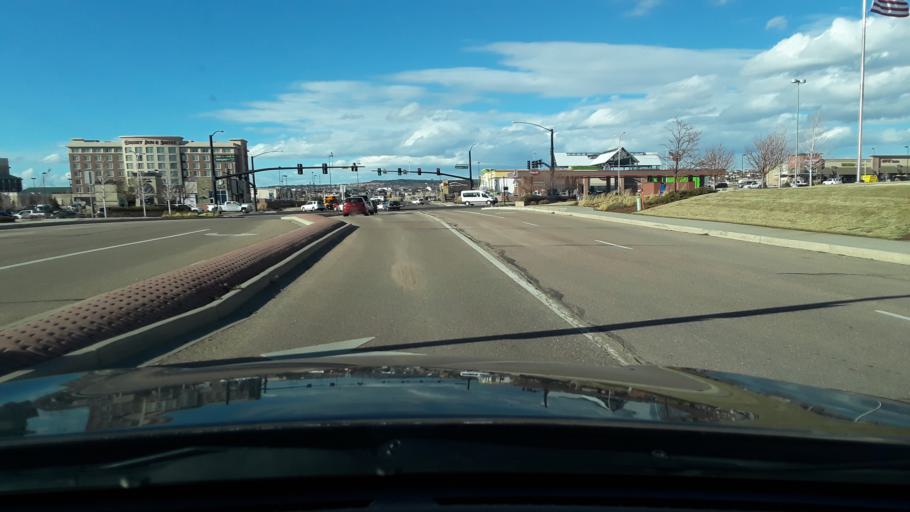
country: US
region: Colorado
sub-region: El Paso County
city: Air Force Academy
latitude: 38.9898
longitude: -104.8077
